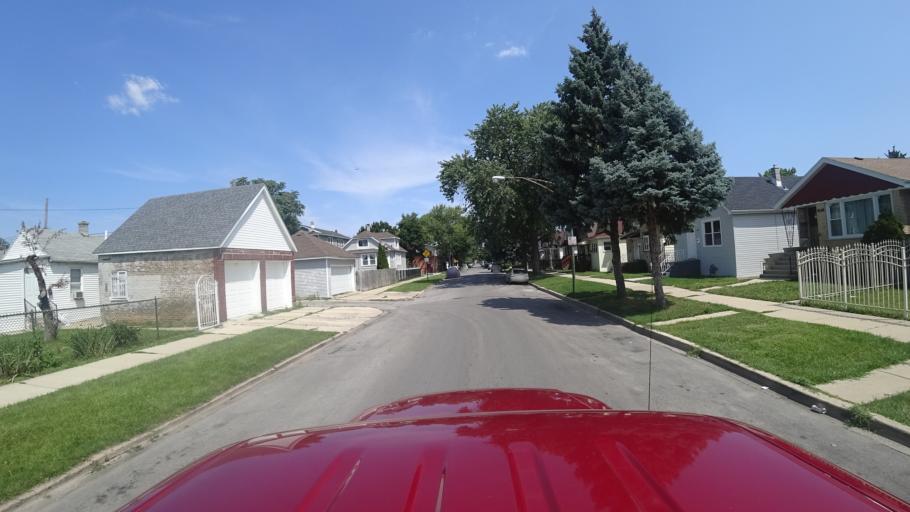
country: US
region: Illinois
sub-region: Cook County
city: Hometown
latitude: 41.7956
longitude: -87.6988
